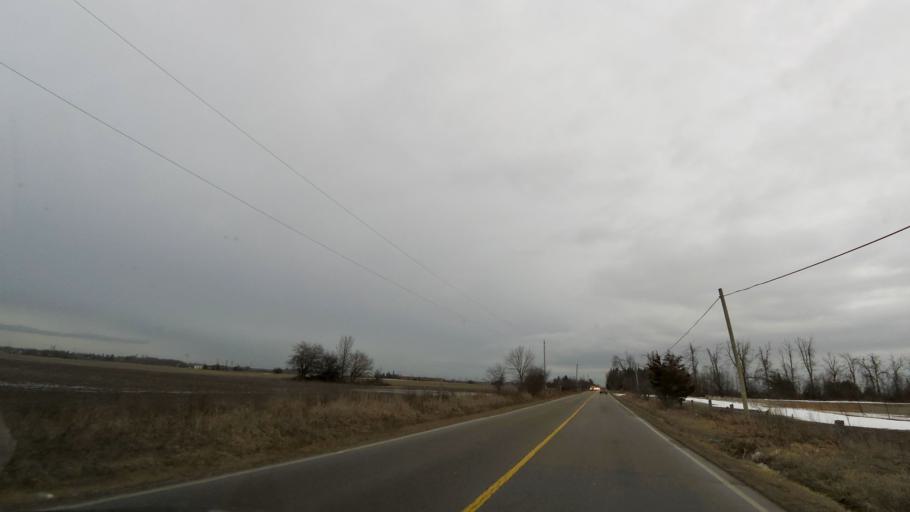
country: CA
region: Ontario
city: Brampton
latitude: 43.8302
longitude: -79.6942
